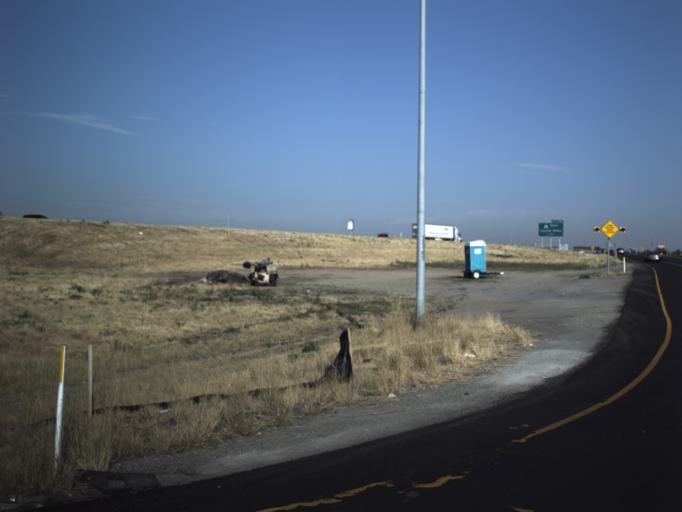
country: US
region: Utah
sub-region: Davis County
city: Kaysville
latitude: 41.0384
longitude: -111.9474
